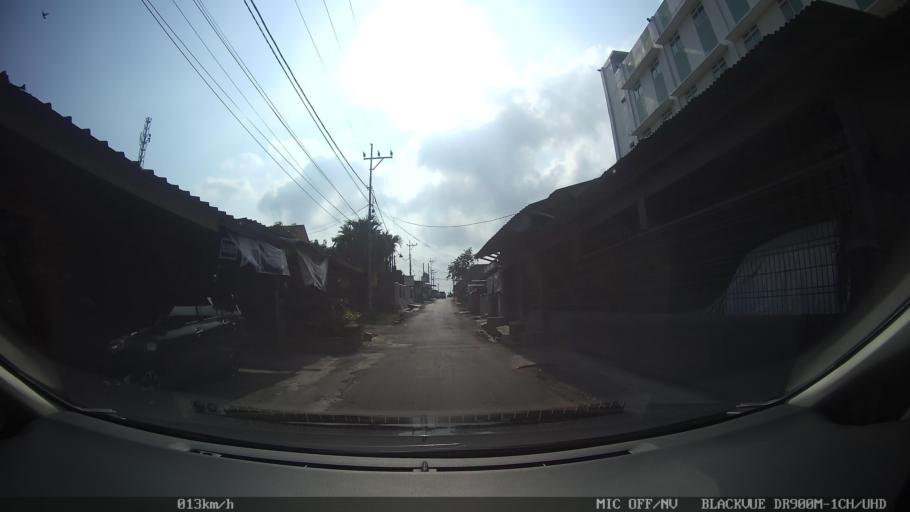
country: ID
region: Lampung
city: Kedaton
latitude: -5.3912
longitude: 105.2621
